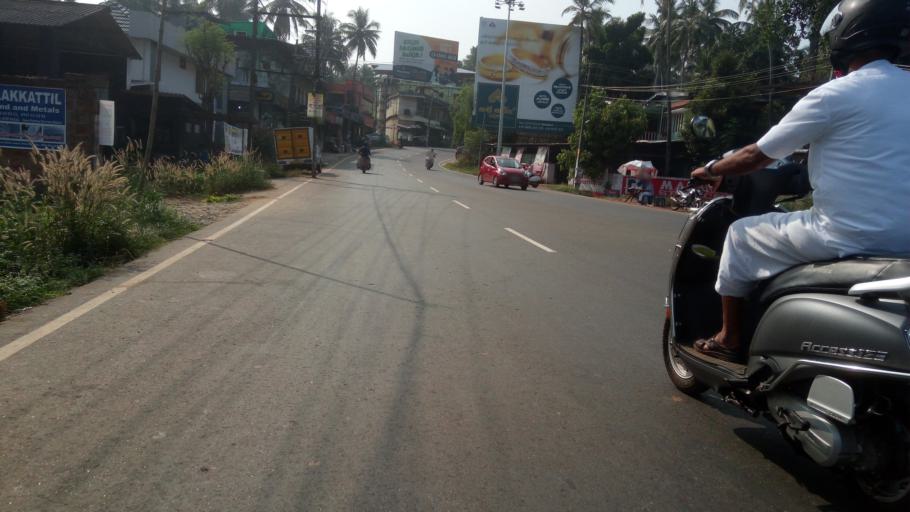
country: IN
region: Kerala
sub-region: Malappuram
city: Malappuram
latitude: 11.0035
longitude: 76.0121
